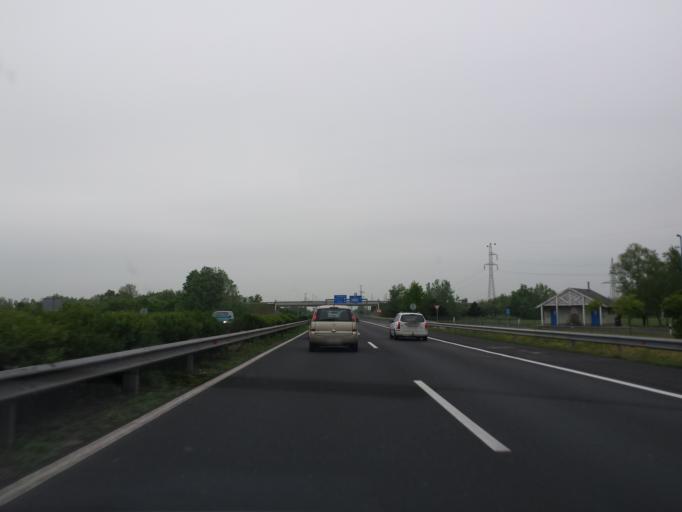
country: HU
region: Gyor-Moson-Sopron
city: Mosonmagyarovar
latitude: 47.8454
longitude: 17.2571
